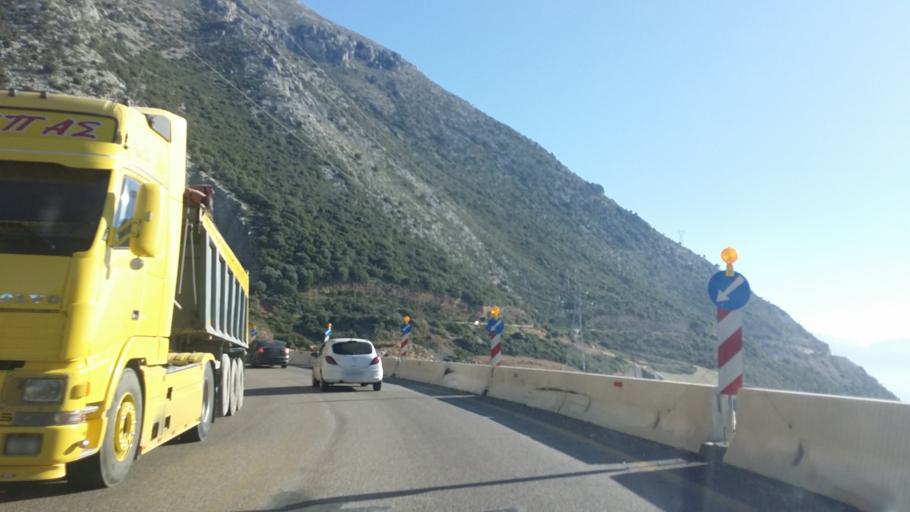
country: GR
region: West Greece
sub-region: Nomos Aitolias kai Akarnanias
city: Galatas
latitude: 38.3575
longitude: 21.6607
